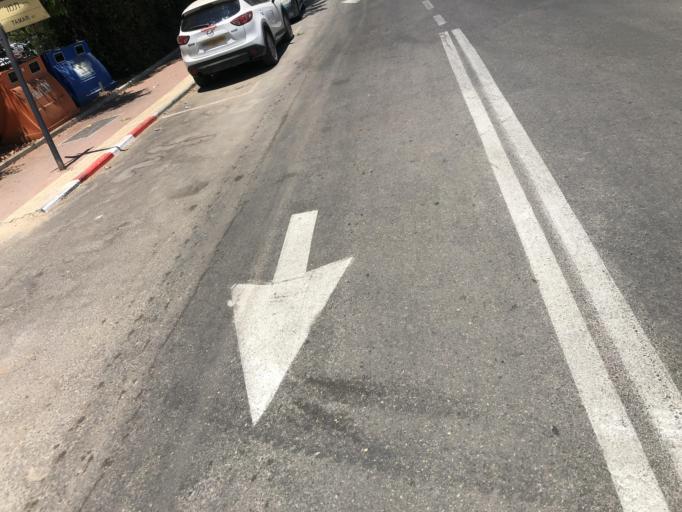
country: IL
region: Tel Aviv
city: Or Yehuda
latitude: 32.0281
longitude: 34.8748
